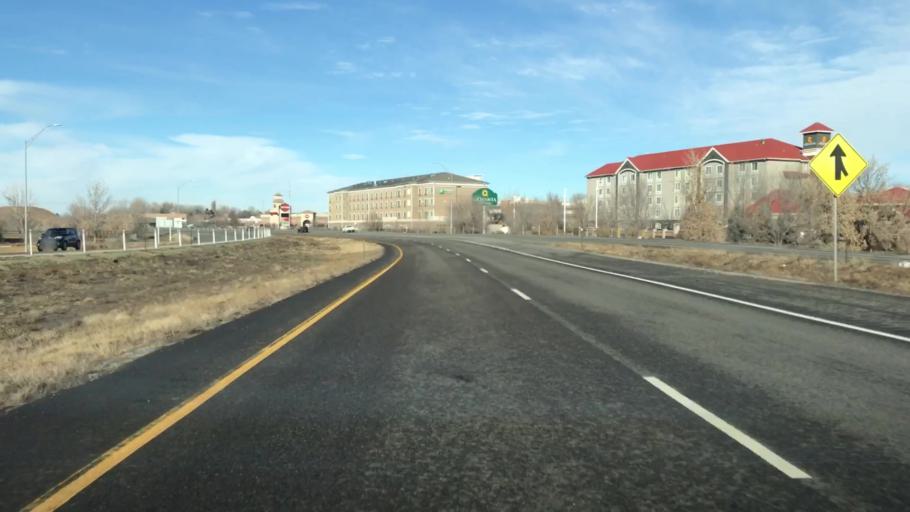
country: US
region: Colorado
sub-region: Mesa County
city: Grand Junction
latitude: 39.1131
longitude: -108.5408
